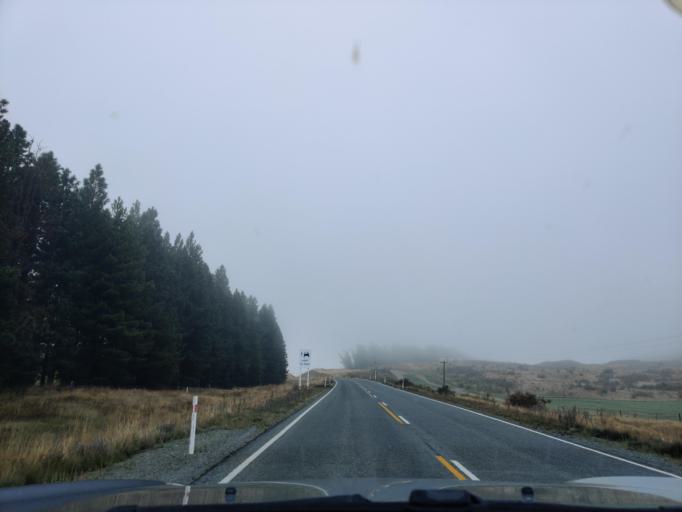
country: NZ
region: Canterbury
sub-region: Timaru District
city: Pleasant Point
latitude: -44.1940
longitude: 170.2859
